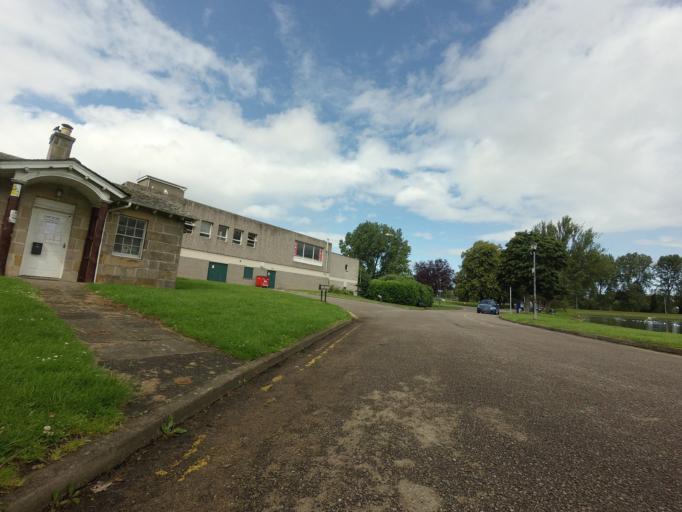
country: GB
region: Scotland
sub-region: Moray
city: Elgin
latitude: 57.6508
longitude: -3.3137
